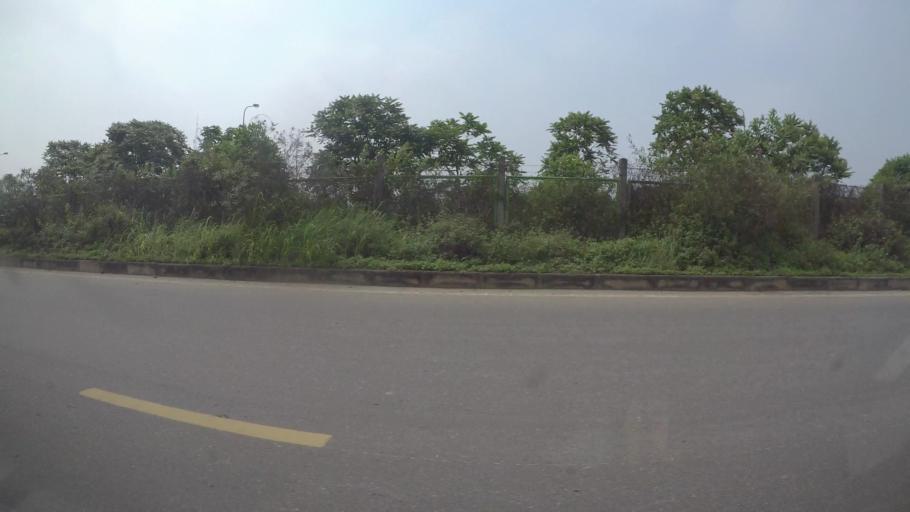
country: VN
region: Ha Noi
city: Lien Quan
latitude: 20.9909
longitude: 105.5514
